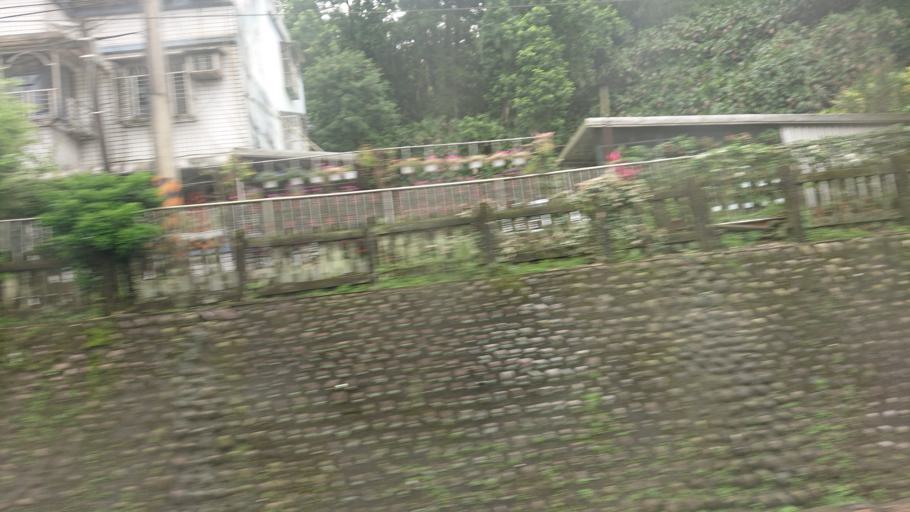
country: TW
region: Taiwan
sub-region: Keelung
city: Keelung
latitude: 25.0849
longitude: 121.7054
